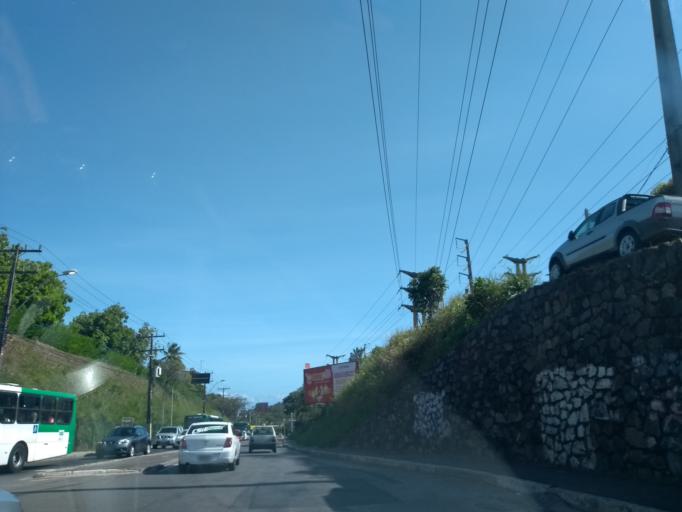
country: BR
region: Bahia
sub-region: Salvador
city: Salvador
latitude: -12.9394
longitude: -38.4215
